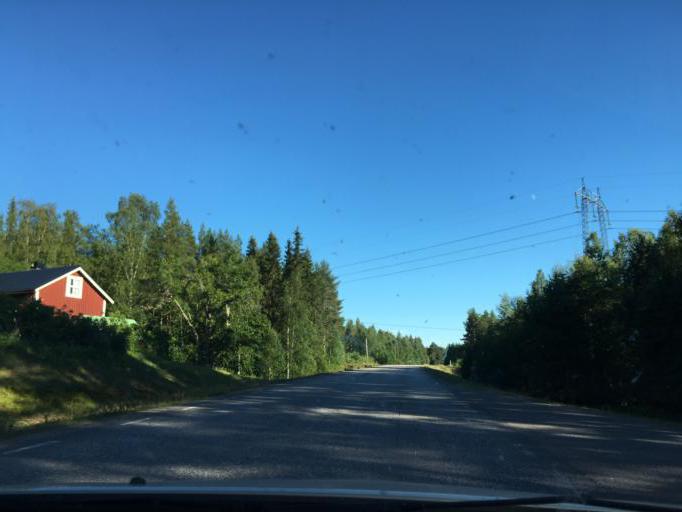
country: SE
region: Norrbotten
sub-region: Kalix Kommun
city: Rolfs
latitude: 65.9108
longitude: 22.9281
